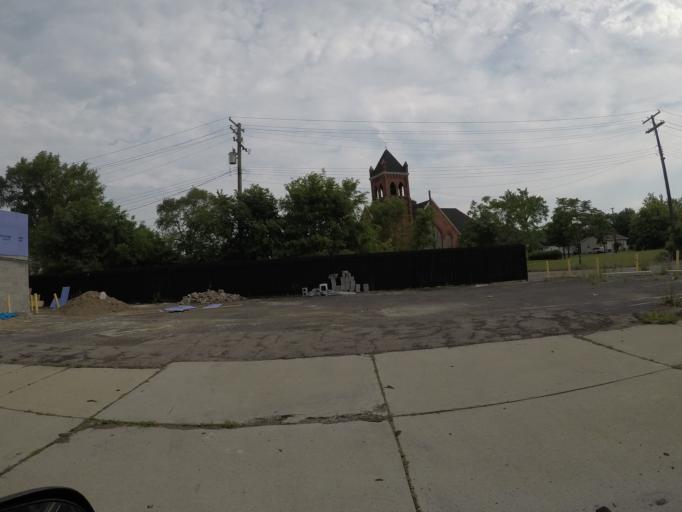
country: US
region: Michigan
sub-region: Wayne County
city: Detroit
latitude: 42.3316
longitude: -83.0923
